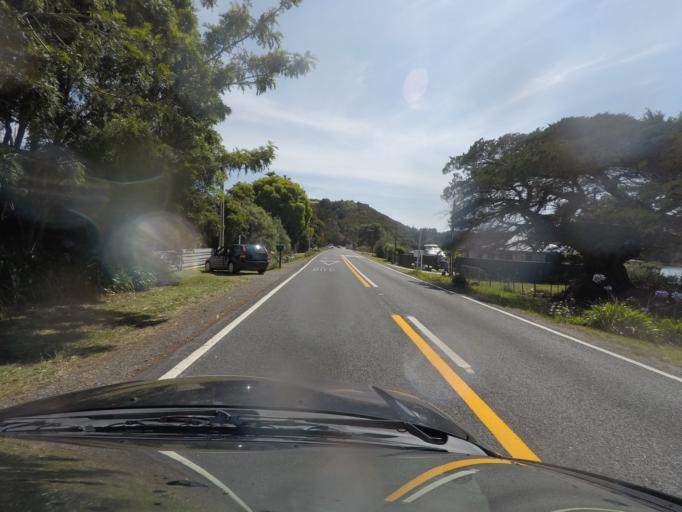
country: NZ
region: Auckland
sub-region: Auckland
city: Warkworth
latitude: -36.3093
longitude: 174.7772
